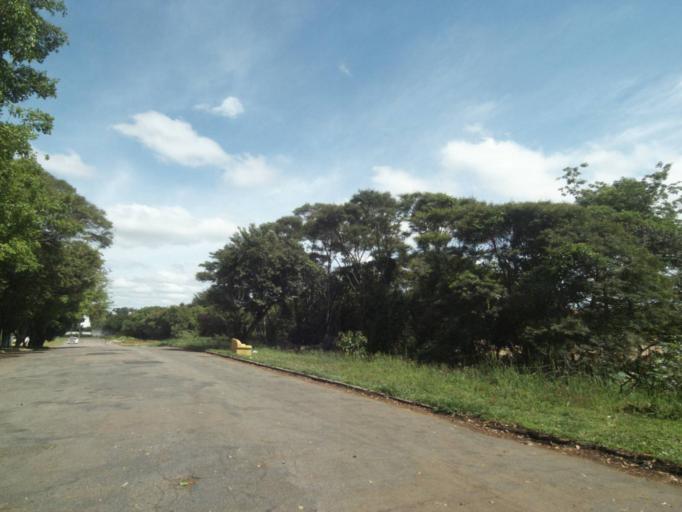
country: BR
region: Parana
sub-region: Curitiba
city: Curitiba
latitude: -25.4920
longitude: -49.3296
